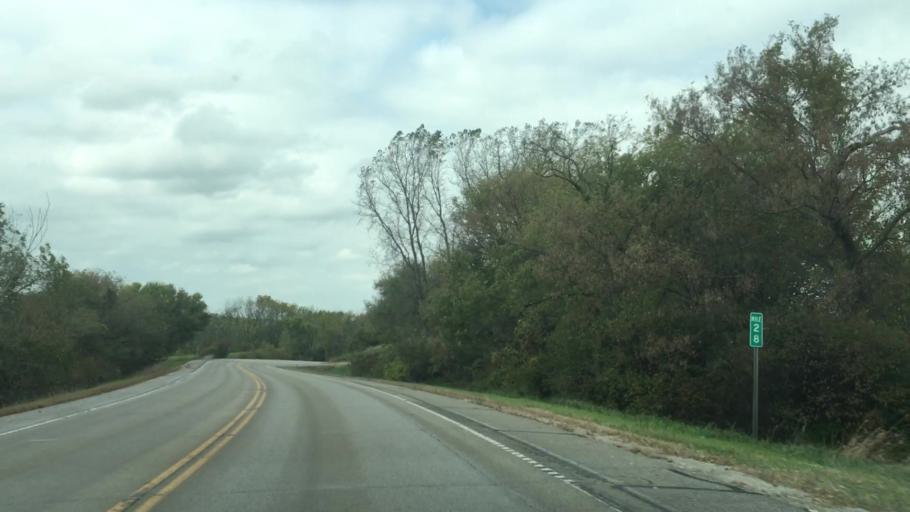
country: US
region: Minnesota
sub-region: Fillmore County
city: Chatfield
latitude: 43.7805
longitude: -92.1313
